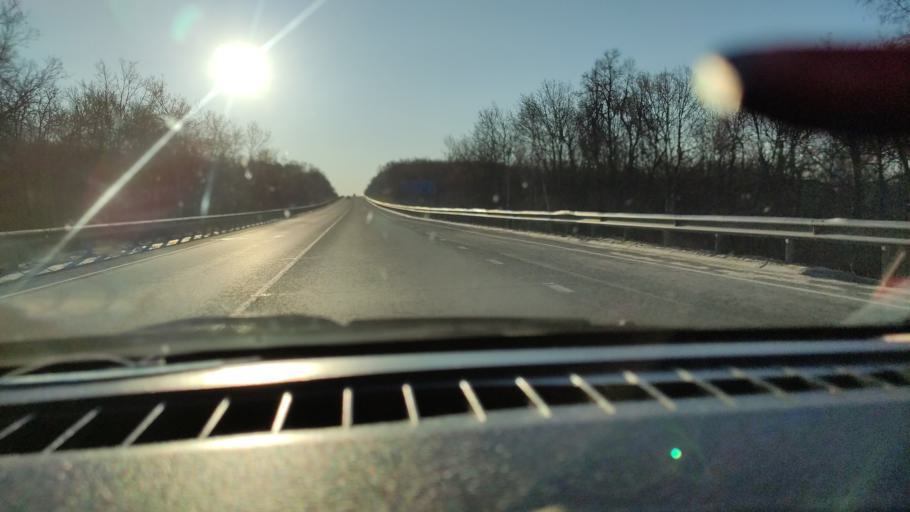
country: RU
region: Saratov
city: Vol'sk
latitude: 52.1085
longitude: 47.3896
